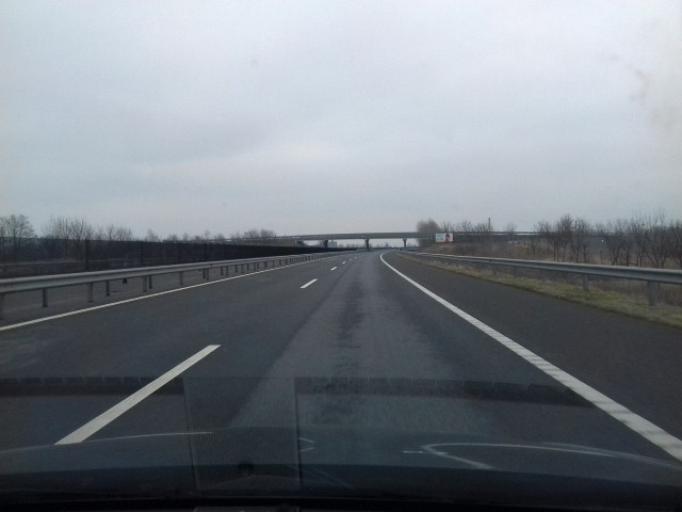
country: HU
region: Szabolcs-Szatmar-Bereg
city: Nyiregyhaza
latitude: 47.9015
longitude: 21.6640
